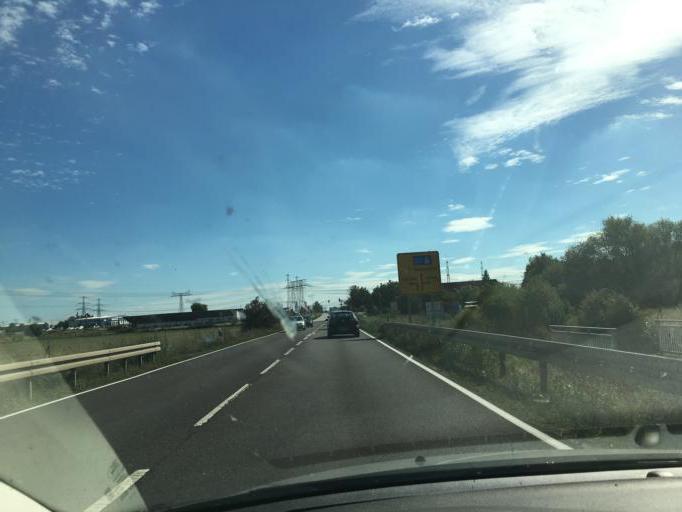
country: DE
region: Saxony-Anhalt
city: Wolmirstedt
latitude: 52.2784
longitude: 11.6272
